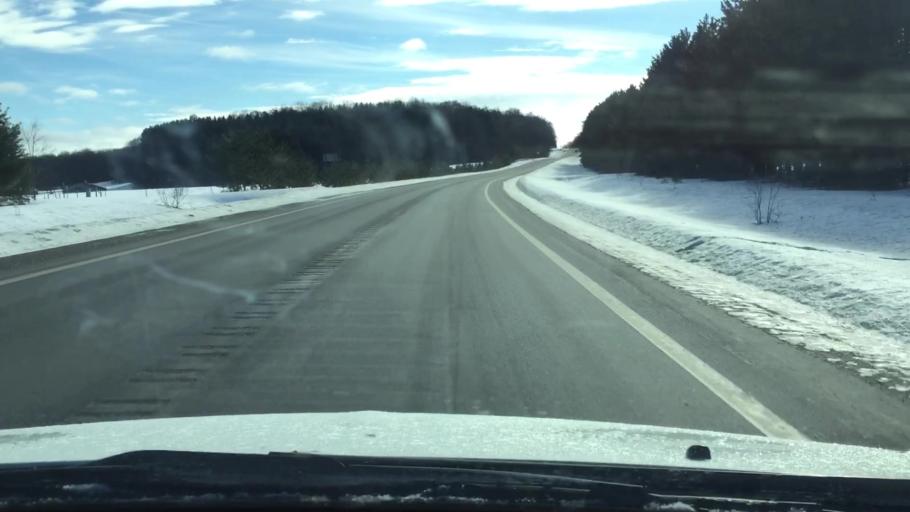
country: US
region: Michigan
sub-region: Antrim County
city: Mancelona
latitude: 44.9811
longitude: -85.0537
